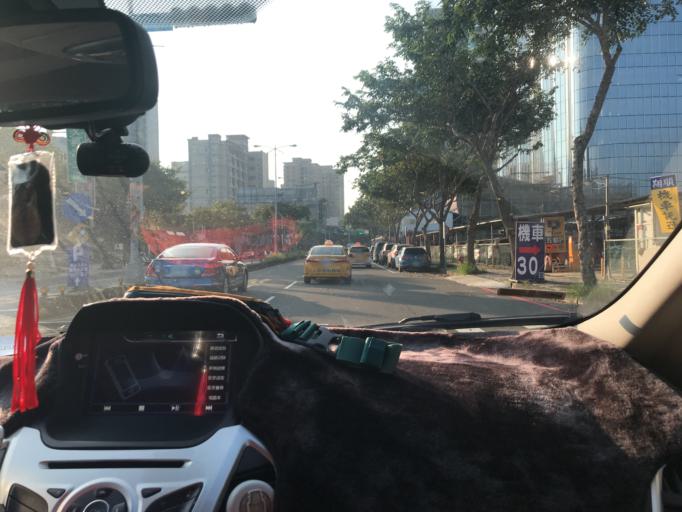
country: TW
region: Taiwan
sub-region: Hsinchu
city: Zhubei
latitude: 24.8063
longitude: 121.0390
